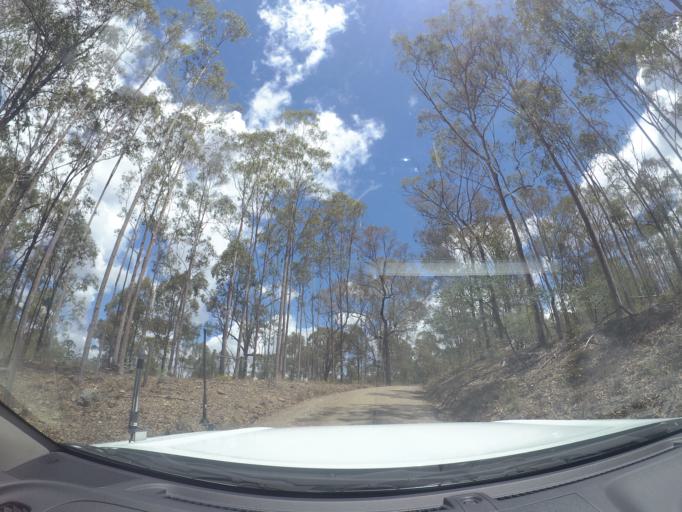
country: AU
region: Queensland
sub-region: Logan
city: Cedar Vale
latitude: -27.9165
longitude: 153.0484
